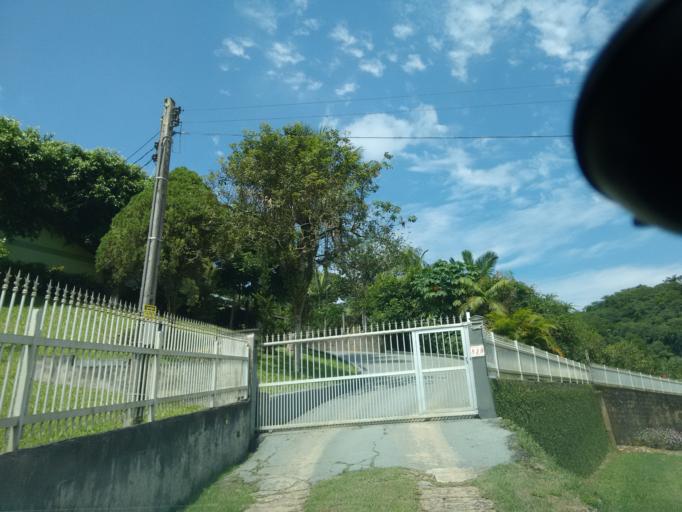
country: BR
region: Santa Catarina
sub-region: Indaial
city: Indaial
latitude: -26.8507
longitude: -49.1638
